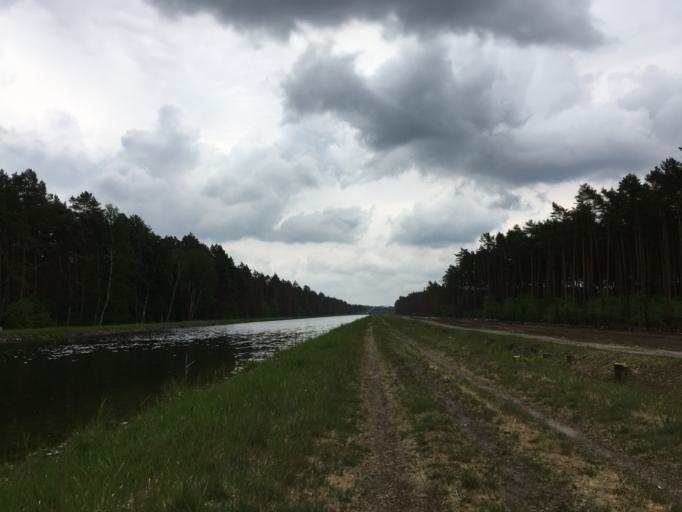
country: DE
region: Brandenburg
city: Marienwerder
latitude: 52.8525
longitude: 13.6285
